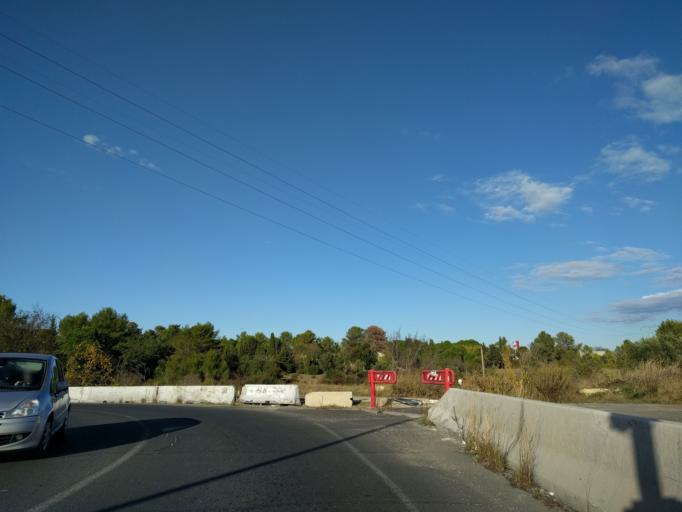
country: FR
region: Languedoc-Roussillon
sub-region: Departement de l'Herault
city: Montferrier-sur-Lez
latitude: 43.6465
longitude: 3.8445
